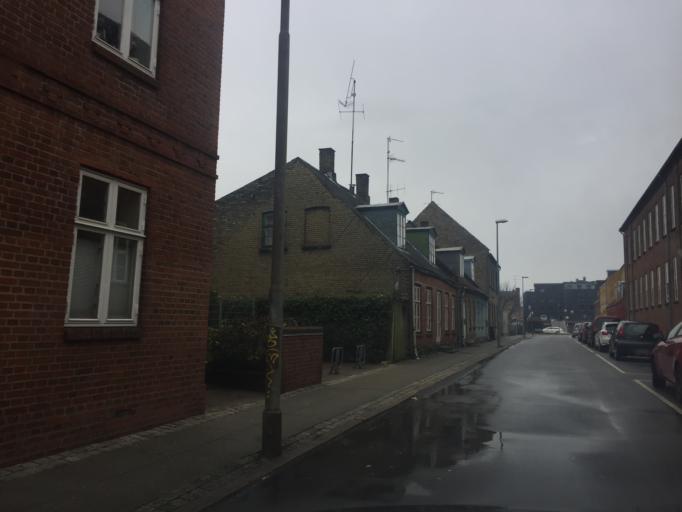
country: DK
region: Zealand
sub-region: Roskilde Kommune
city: Roskilde
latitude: 55.6393
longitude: 12.0831
